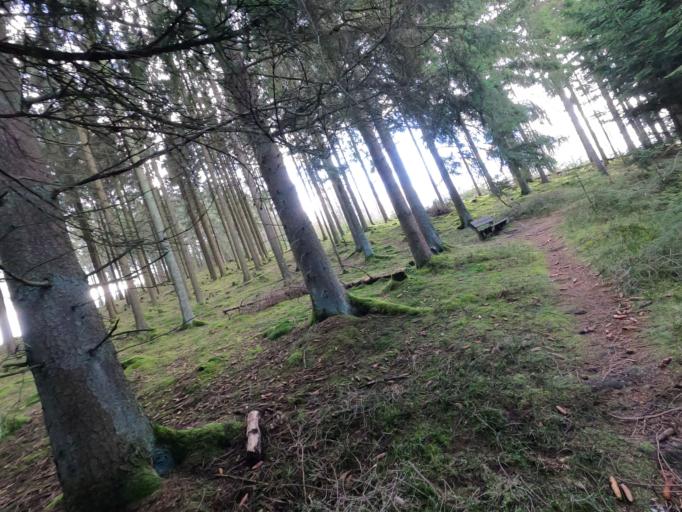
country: DE
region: North Rhine-Westphalia
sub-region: Regierungsbezirk Arnsberg
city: Herscheid
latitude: 51.1786
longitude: 7.7614
